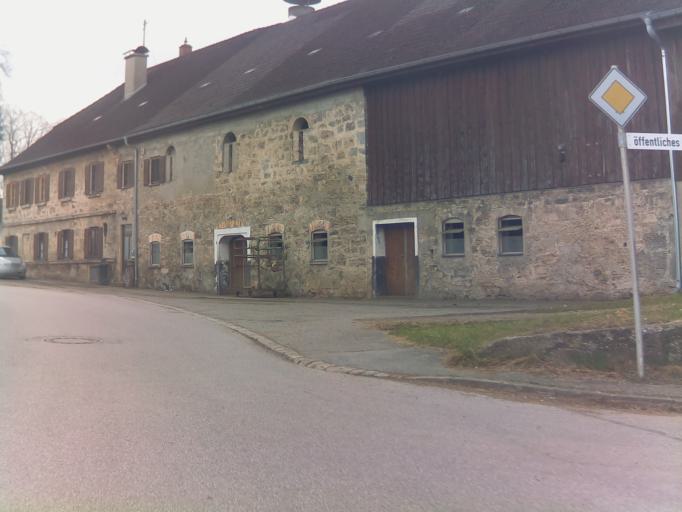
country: DE
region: Bavaria
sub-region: Upper Bavaria
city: Wessobrunn
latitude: 47.8472
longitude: 11.0289
